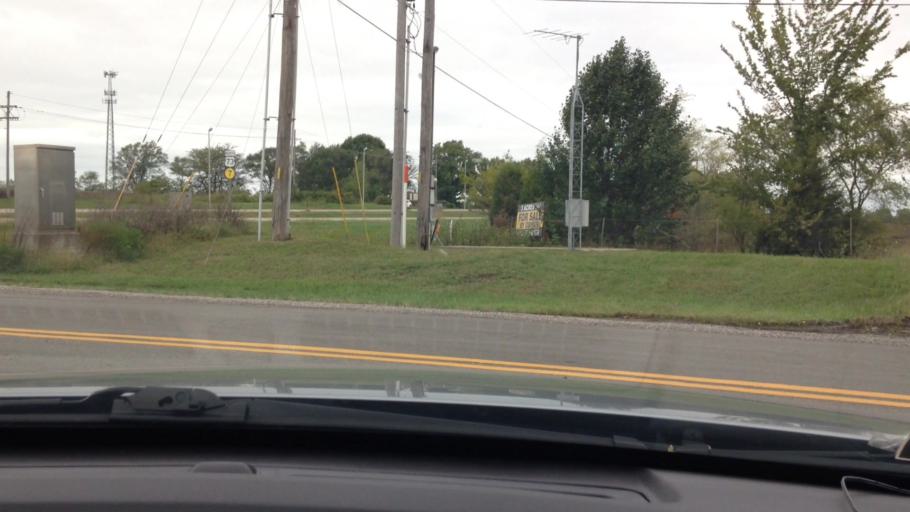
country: US
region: Kansas
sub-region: Leavenworth County
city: Basehor
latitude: 39.1869
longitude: -94.8994
